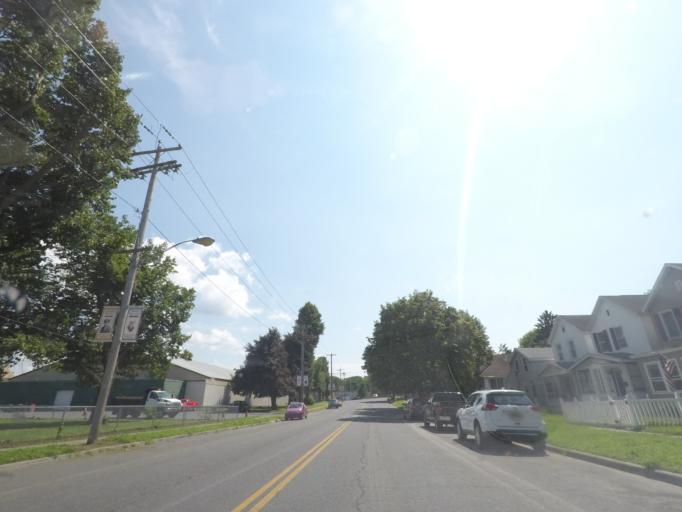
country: US
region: New York
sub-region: Albany County
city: Watervliet
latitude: 42.7246
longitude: -73.7030
